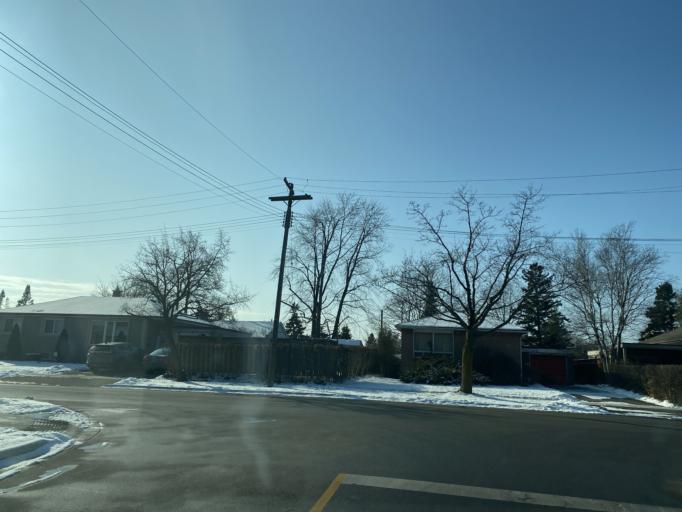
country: CA
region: Ontario
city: Etobicoke
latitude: 43.6652
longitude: -79.5619
